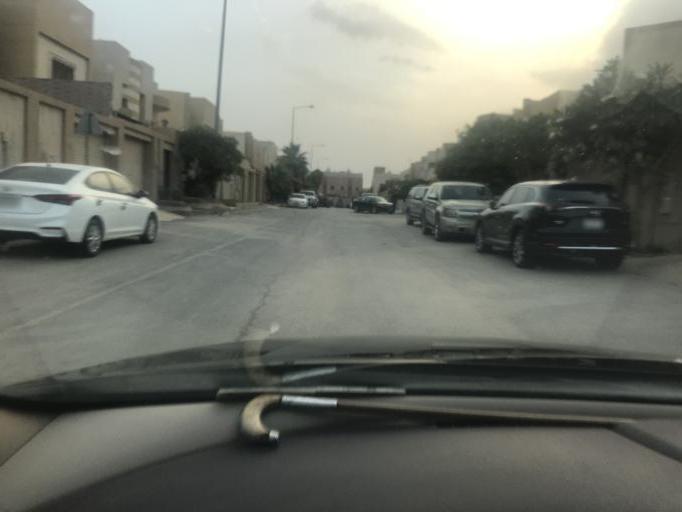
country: SA
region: Ar Riyad
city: Riyadh
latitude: 24.7303
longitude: 46.7462
